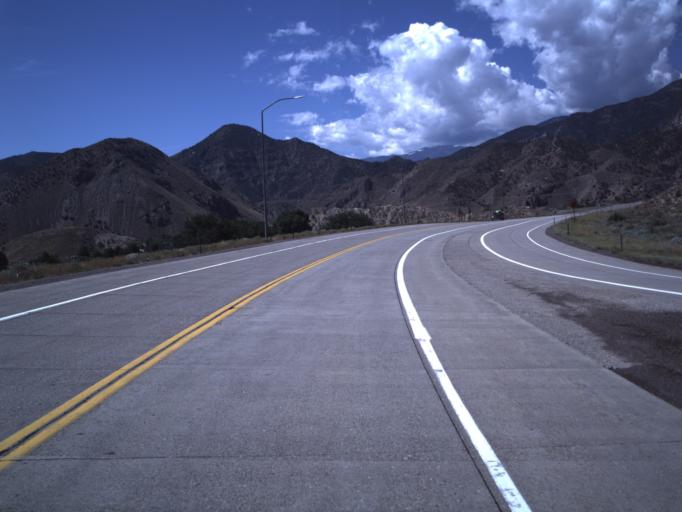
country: US
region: Utah
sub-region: Sevier County
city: Monroe
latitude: 38.5952
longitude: -112.2544
